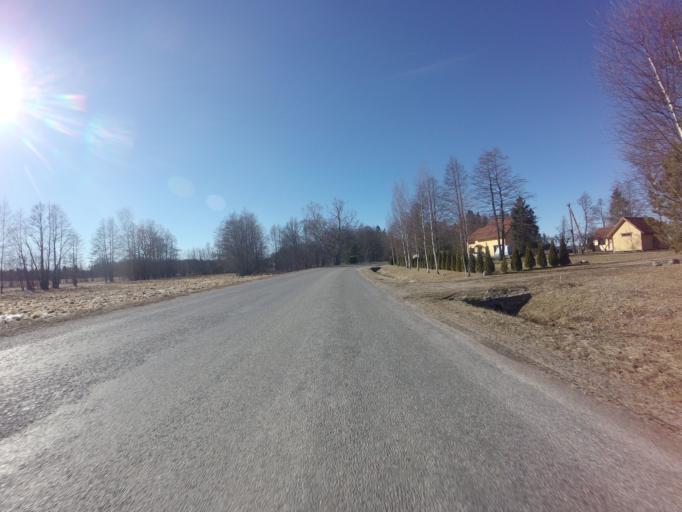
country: EE
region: Saare
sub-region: Kuressaare linn
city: Kuressaare
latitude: 58.5750
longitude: 22.6468
